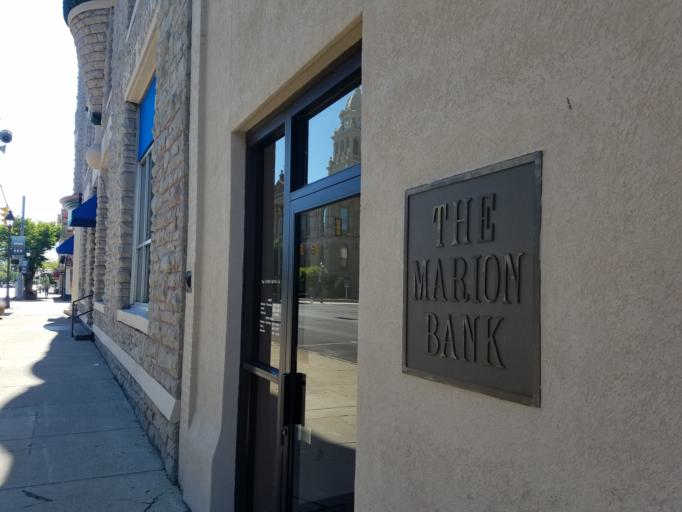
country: US
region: Ohio
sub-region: Marion County
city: Marion
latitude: 40.5888
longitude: -83.1295
